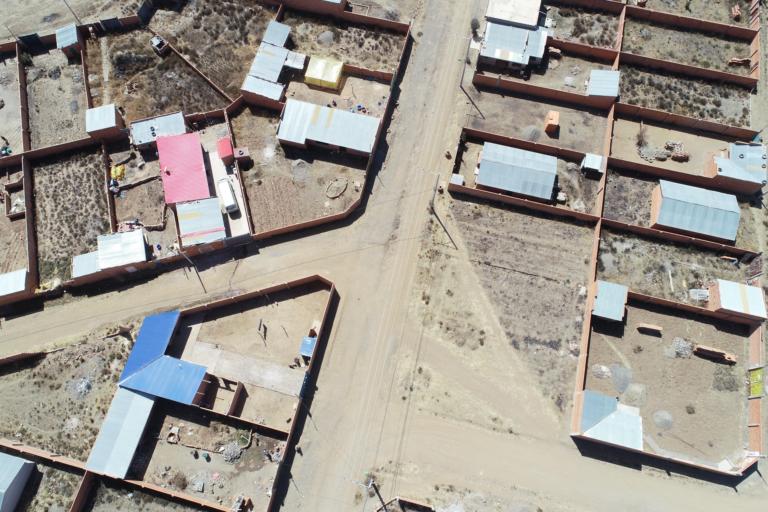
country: BO
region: La Paz
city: La Paz
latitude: -16.5936
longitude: -68.2133
